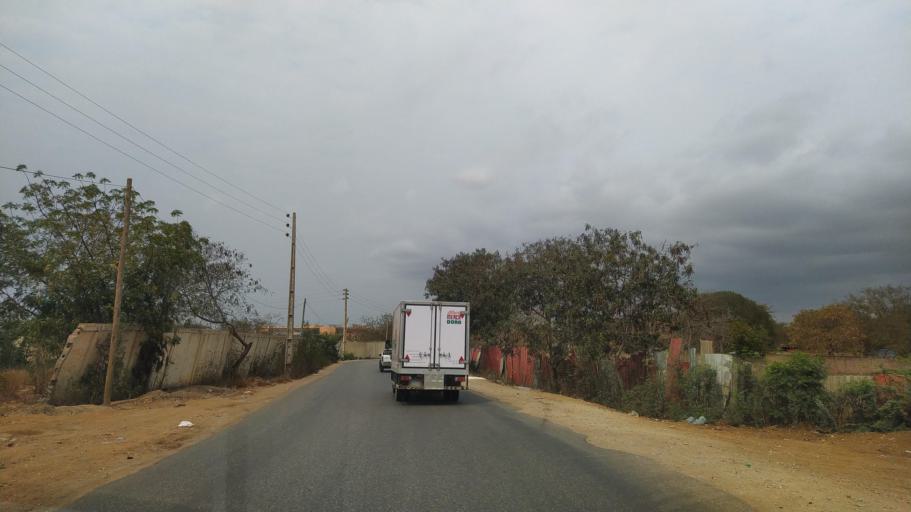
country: AO
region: Luanda
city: Luanda
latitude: -8.8579
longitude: 13.2848
